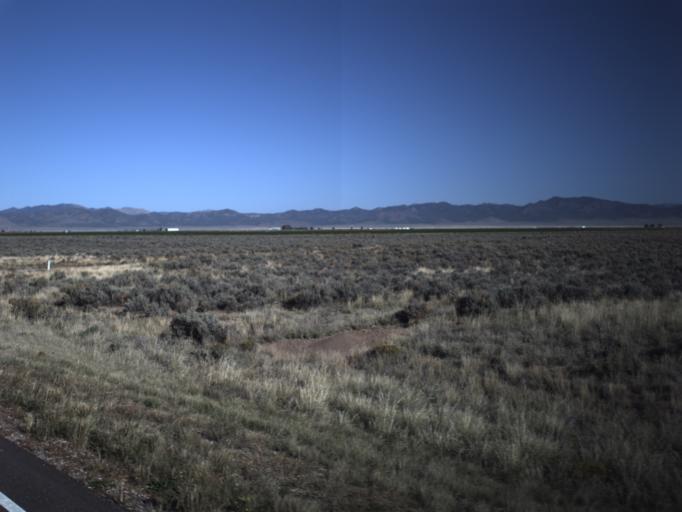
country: US
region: Utah
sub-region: Washington County
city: Enterprise
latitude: 37.7486
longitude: -113.7655
